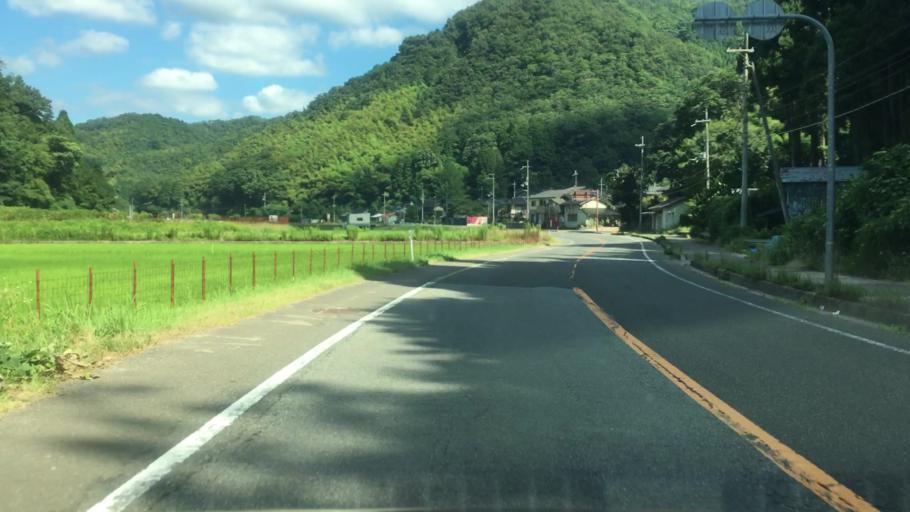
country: JP
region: Hyogo
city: Toyooka
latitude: 35.5690
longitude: 134.7815
